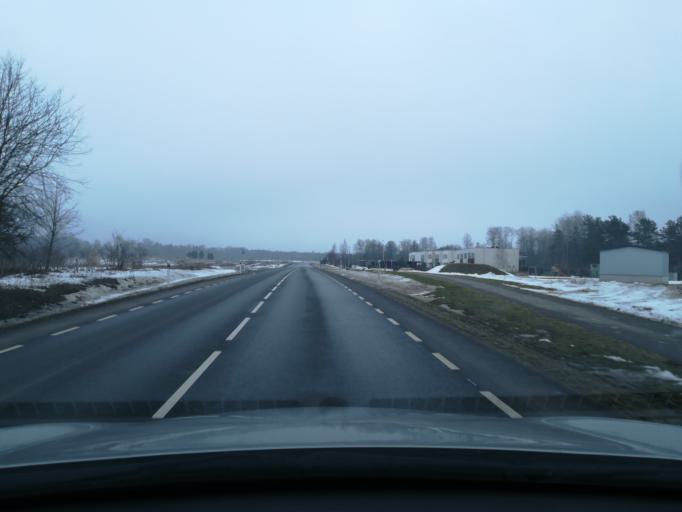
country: EE
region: Harju
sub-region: Kuusalu vald
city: Kuusalu
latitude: 59.4558
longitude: 25.4454
